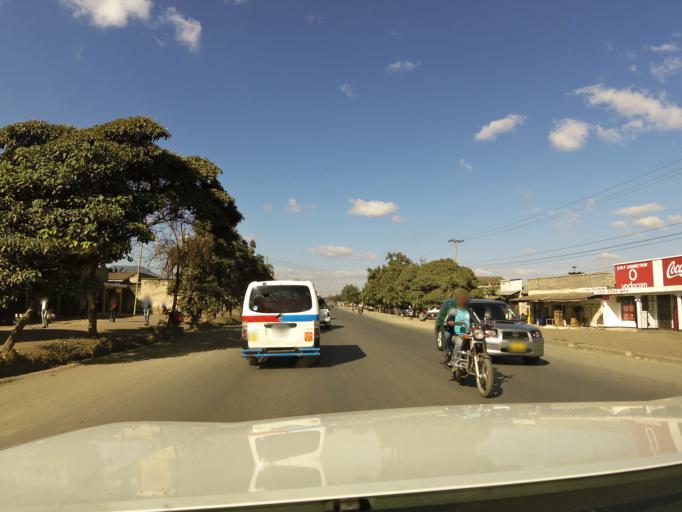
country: TZ
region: Arusha
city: Arusha
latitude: -3.3757
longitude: 36.6697
